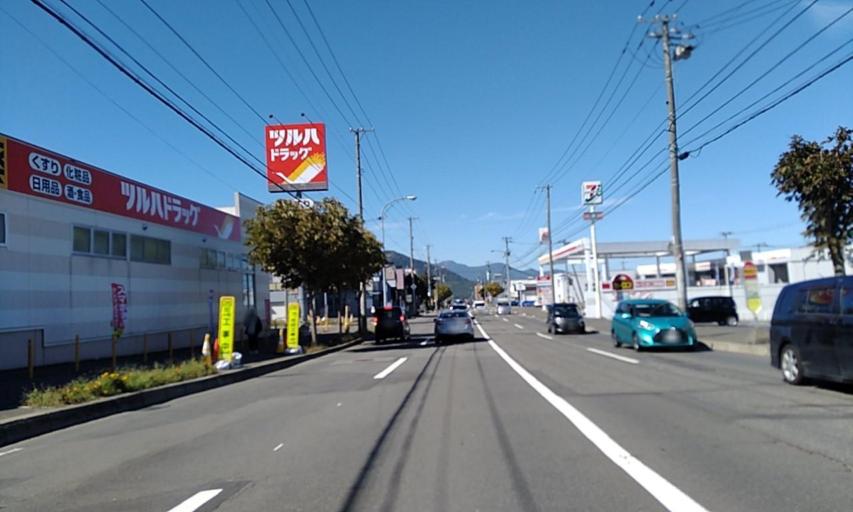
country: JP
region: Hokkaido
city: Sapporo
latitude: 43.0062
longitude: 141.3846
